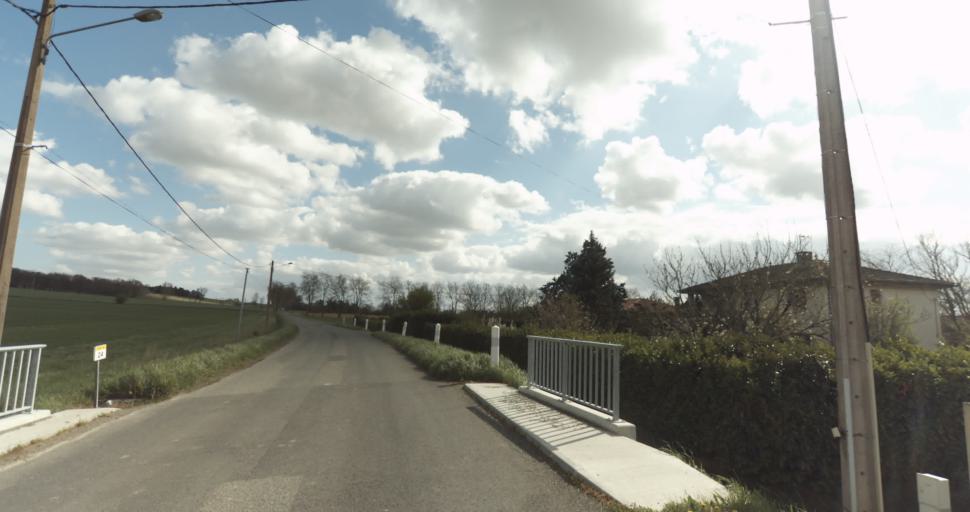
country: FR
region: Midi-Pyrenees
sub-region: Departement de la Haute-Garonne
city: Auterive
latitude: 43.3764
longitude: 1.4636
